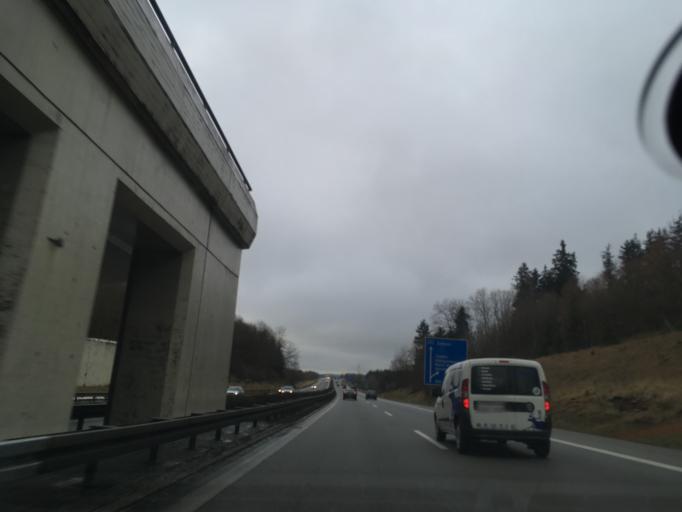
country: DE
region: Bavaria
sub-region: Swabia
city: Stetten
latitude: 48.0321
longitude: 10.4531
